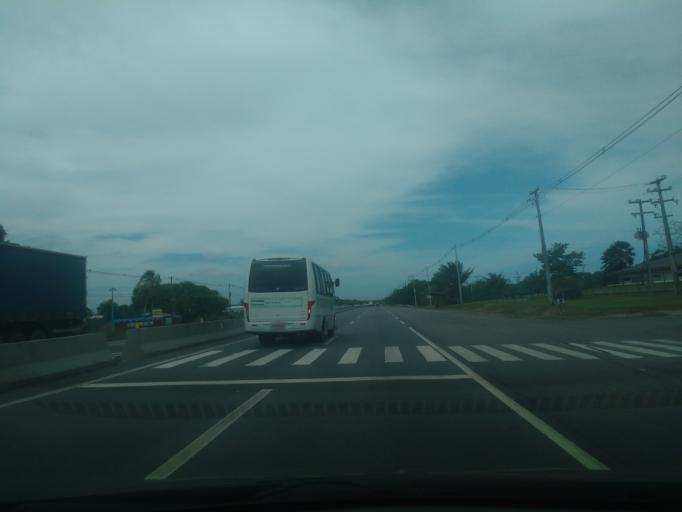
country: BR
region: Alagoas
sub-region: Maceio
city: Maceio
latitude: -9.7019
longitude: -35.8036
